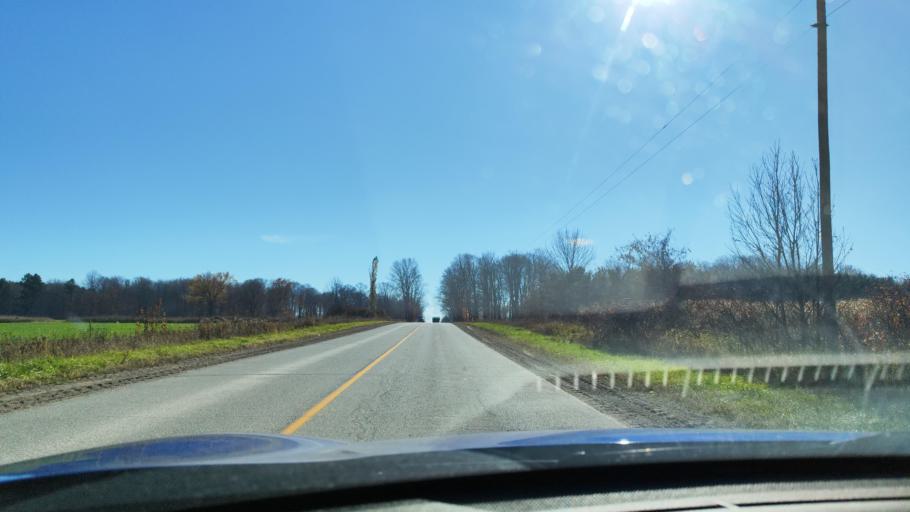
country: CA
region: Ontario
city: Wasaga Beach
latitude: 44.4582
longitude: -80.0029
